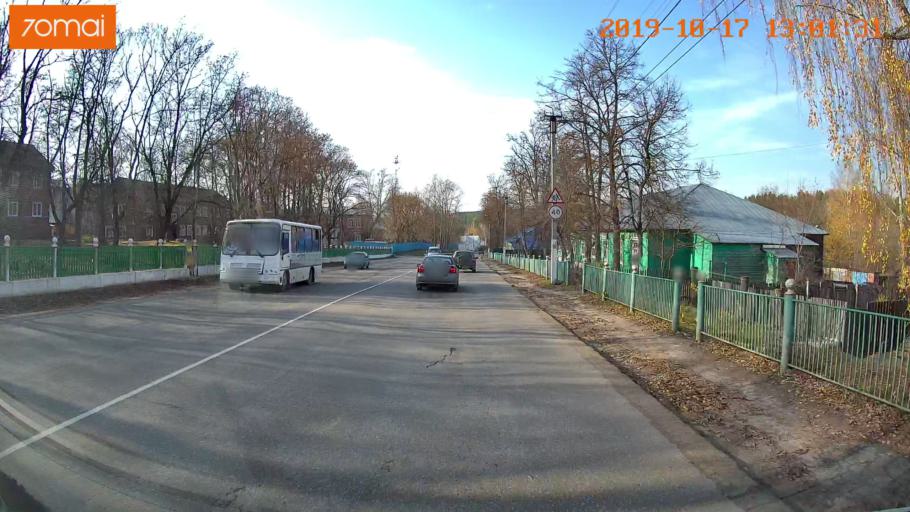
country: RU
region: Rjazan
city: Kasimov
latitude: 54.9458
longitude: 41.3693
